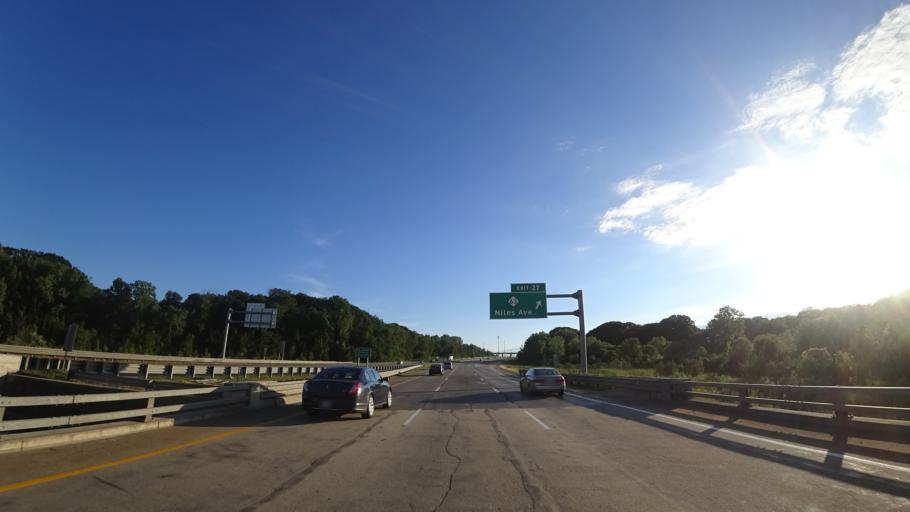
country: US
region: Michigan
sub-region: Berrien County
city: Fair Plain
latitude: 42.0617
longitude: -86.4499
